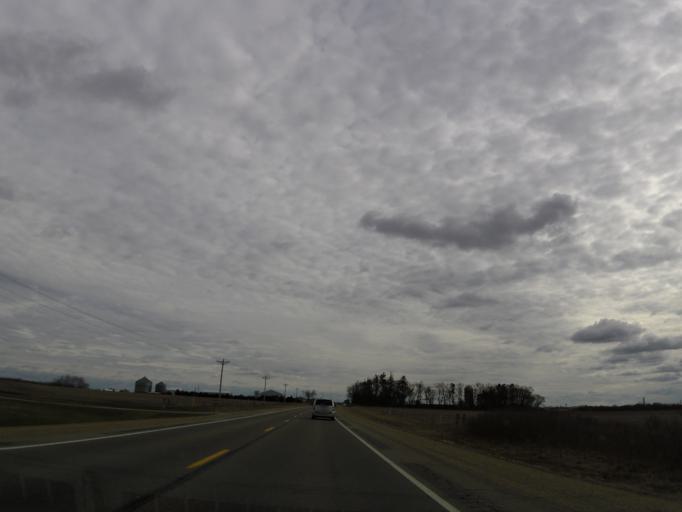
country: US
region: Iowa
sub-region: Chickasaw County
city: New Hampton
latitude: 43.0991
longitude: -92.2978
